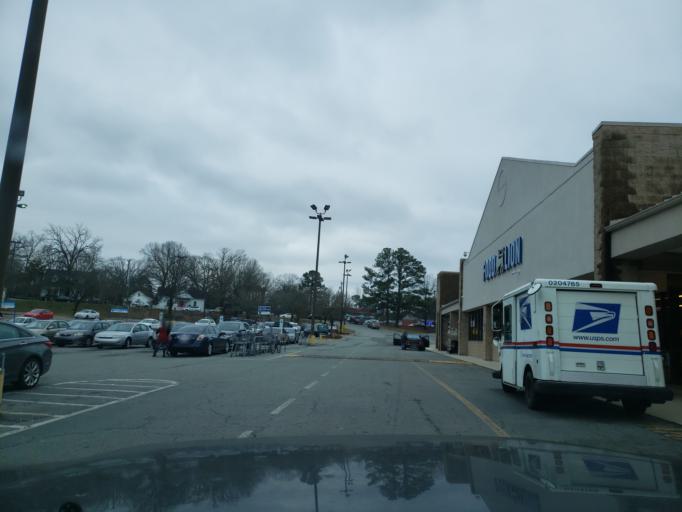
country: US
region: North Carolina
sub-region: Durham County
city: Durham
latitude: 35.9881
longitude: -78.9275
